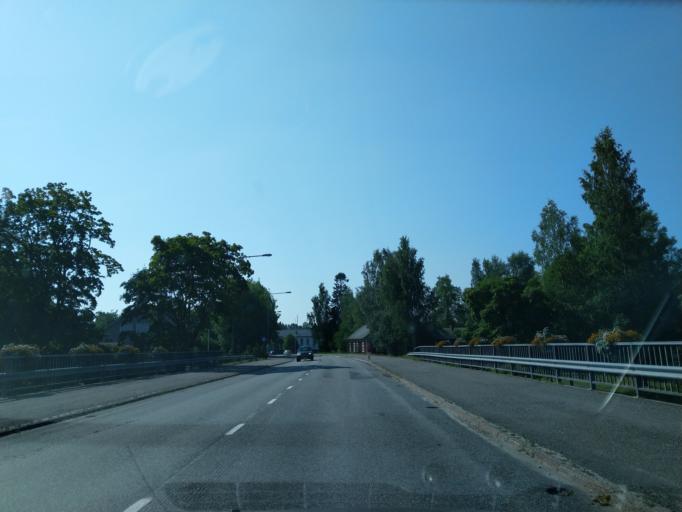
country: FI
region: Satakunta
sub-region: Pori
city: Noormarkku
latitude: 61.5946
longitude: 21.8669
